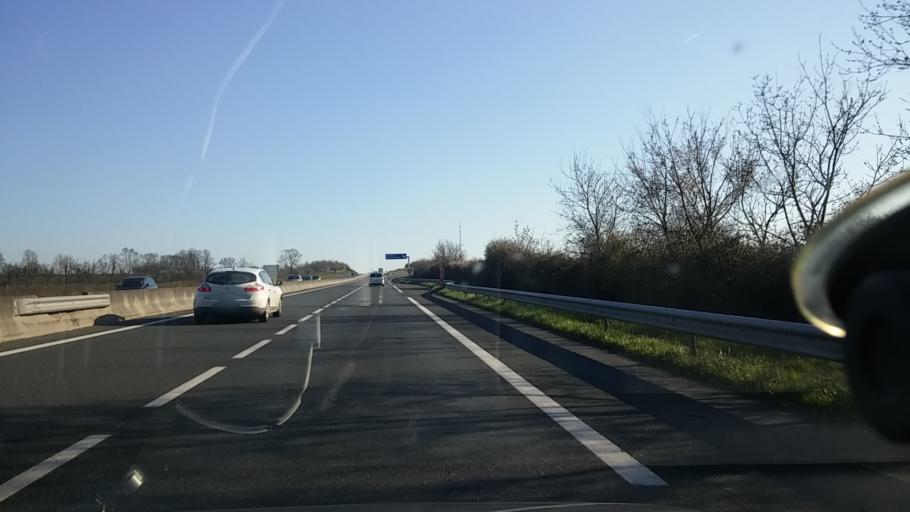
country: FR
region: Centre
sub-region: Departement de l'Indre
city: Argenton-sur-Creuse
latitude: 46.5535
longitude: 1.5060
